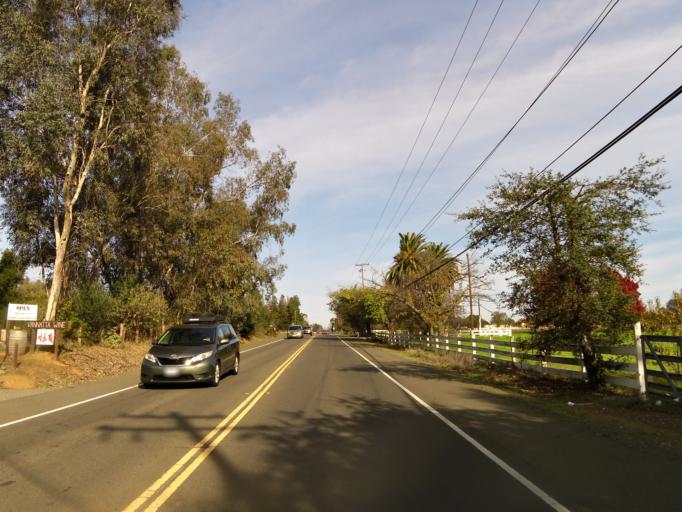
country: US
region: California
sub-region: Sacramento County
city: Wilton
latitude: 38.4407
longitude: -121.2898
